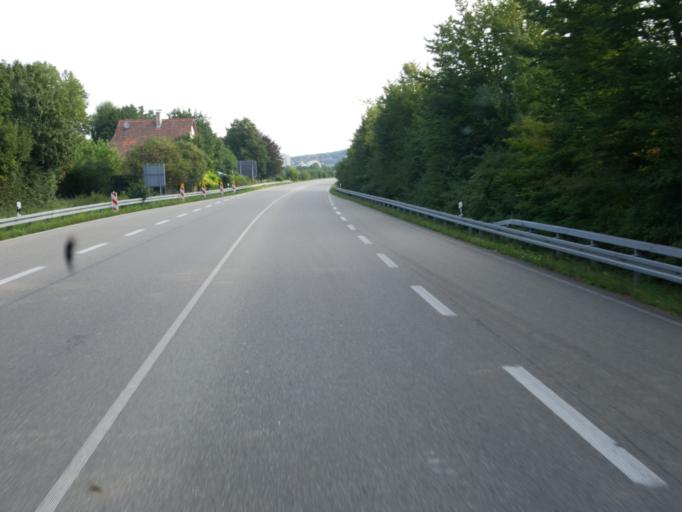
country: DE
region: Baden-Wuerttemberg
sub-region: Freiburg Region
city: Kippenheim
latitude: 48.3266
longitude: 7.8366
